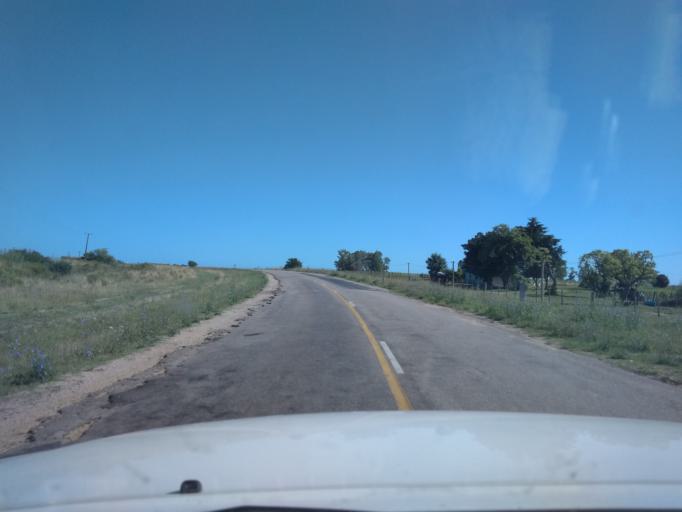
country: UY
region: Canelones
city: San Ramon
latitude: -34.2127
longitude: -55.9291
